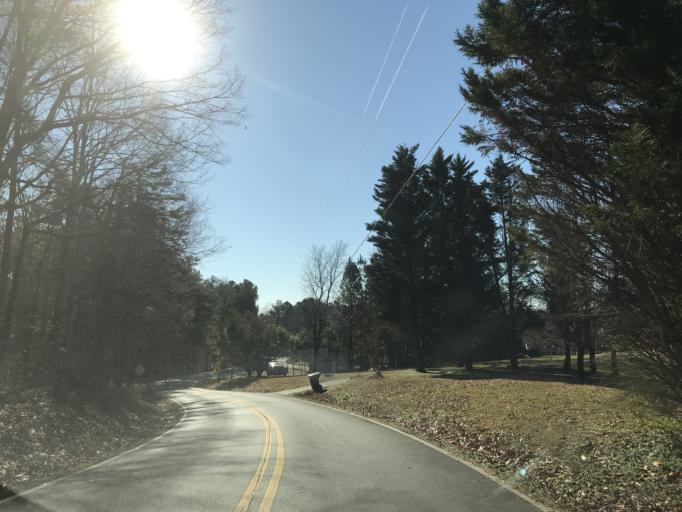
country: US
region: Georgia
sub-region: Paulding County
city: Dallas
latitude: 33.9891
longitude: -84.8941
